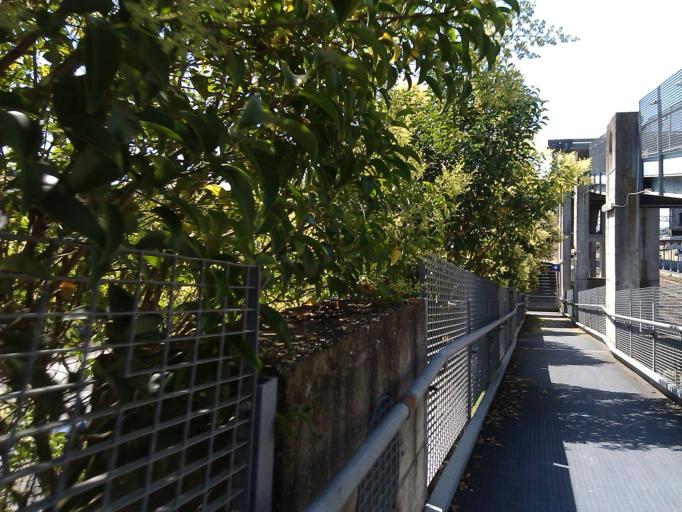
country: IT
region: Umbria
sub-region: Provincia di Terni
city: Fabro Scalo
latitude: 42.8758
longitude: 12.0413
